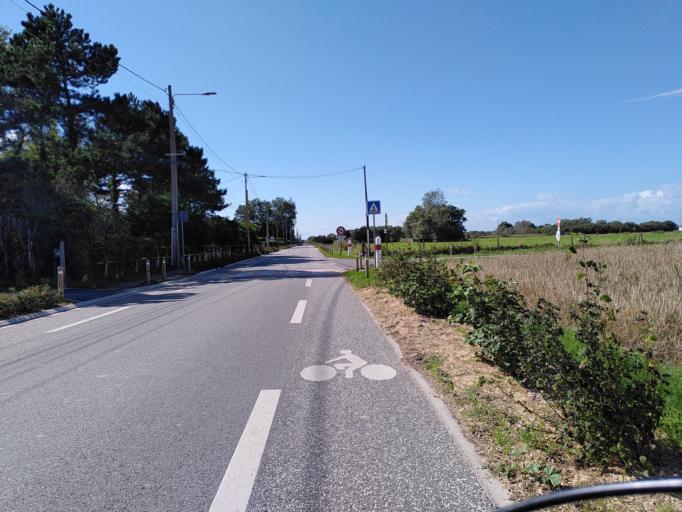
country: FR
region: Nord-Pas-de-Calais
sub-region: Departement du Pas-de-Calais
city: Oye-Plage
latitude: 50.9872
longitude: 2.0557
